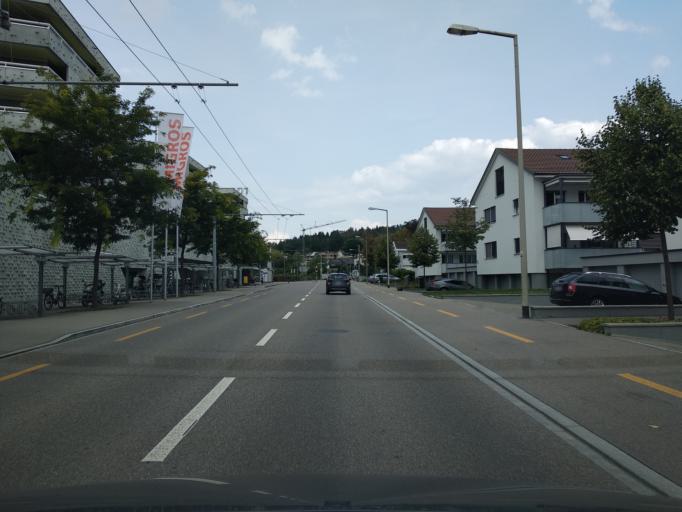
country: CH
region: Zurich
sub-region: Bezirk Winterthur
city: Veltheim
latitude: 47.5179
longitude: 8.7209
